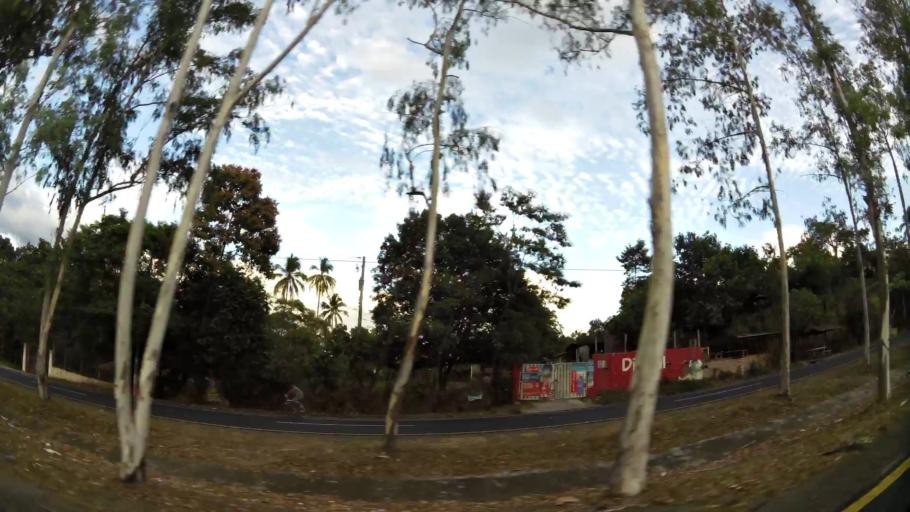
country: SV
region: San Vicente
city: San Sebastian
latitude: 13.6843
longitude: -88.8492
